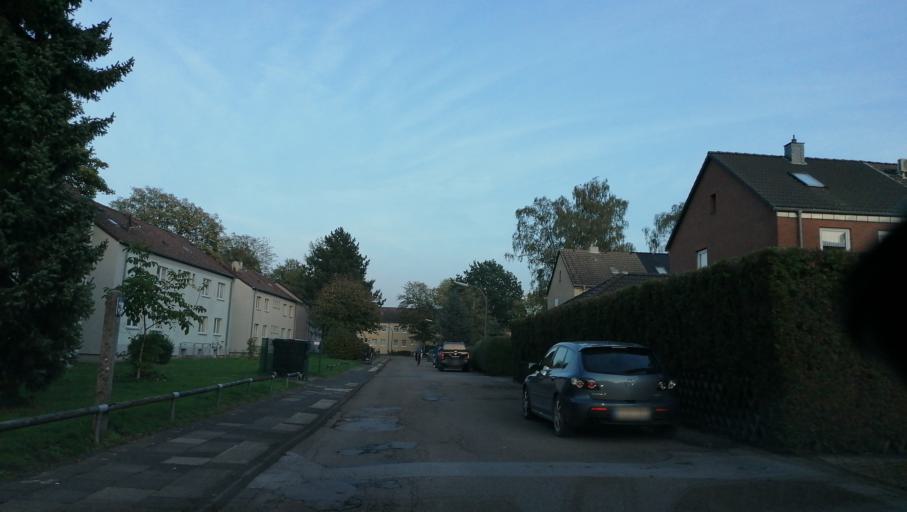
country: DE
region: North Rhine-Westphalia
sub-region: Regierungsbezirk Munster
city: Recklinghausen
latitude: 51.5706
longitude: 7.1828
